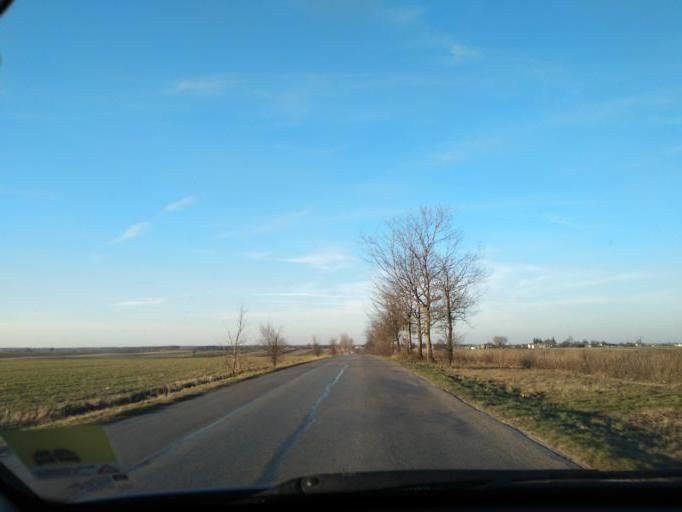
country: PL
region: Lublin Voivodeship
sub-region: Powiat lubartowski
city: Michow
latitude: 51.4980
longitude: 22.3060
